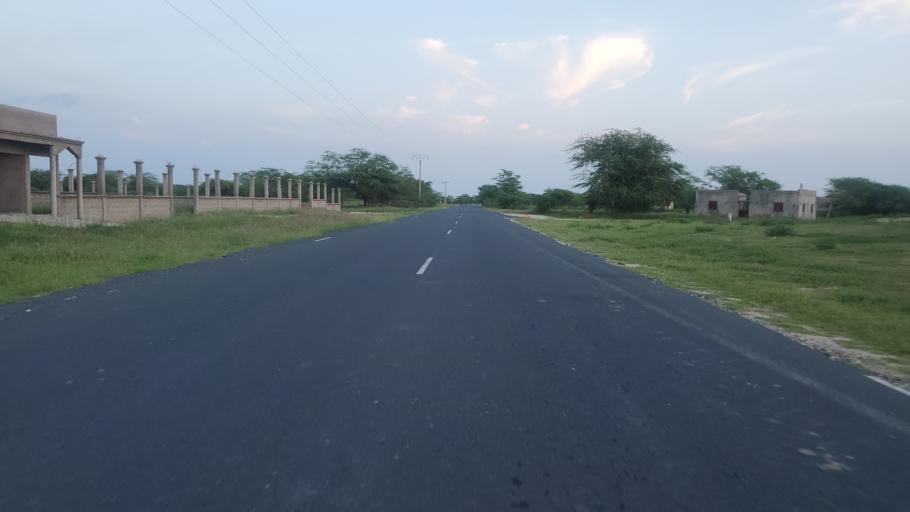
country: SN
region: Saint-Louis
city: Saint-Louis
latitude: 16.1063
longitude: -16.4120
